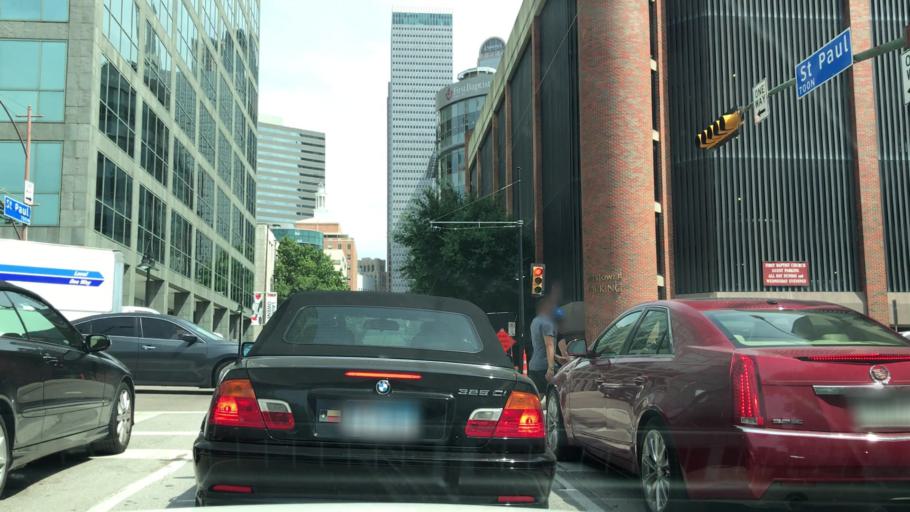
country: US
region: Texas
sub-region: Dallas County
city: Dallas
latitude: 32.7862
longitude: -96.8003
